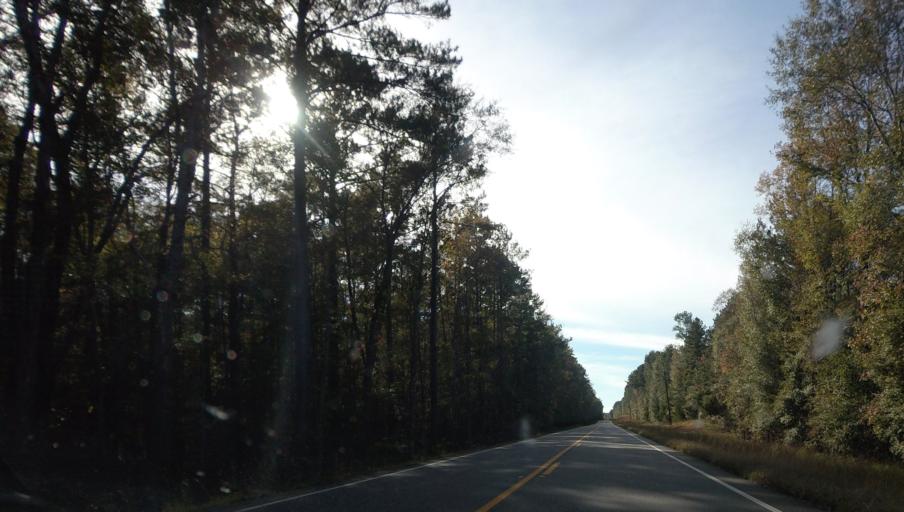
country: US
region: Georgia
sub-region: Taylor County
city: Butler
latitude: 32.7178
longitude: -84.2568
